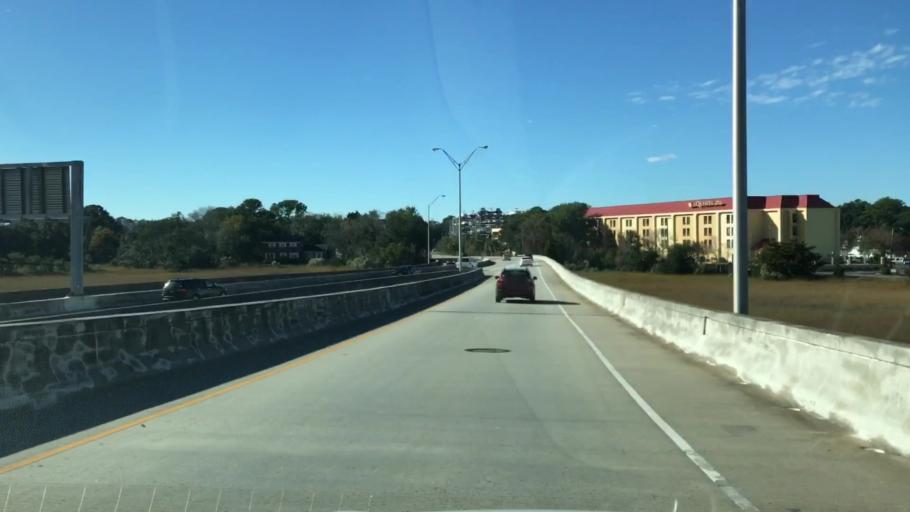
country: US
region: South Carolina
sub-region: Charleston County
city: Charleston
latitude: 32.7764
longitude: -79.9601
